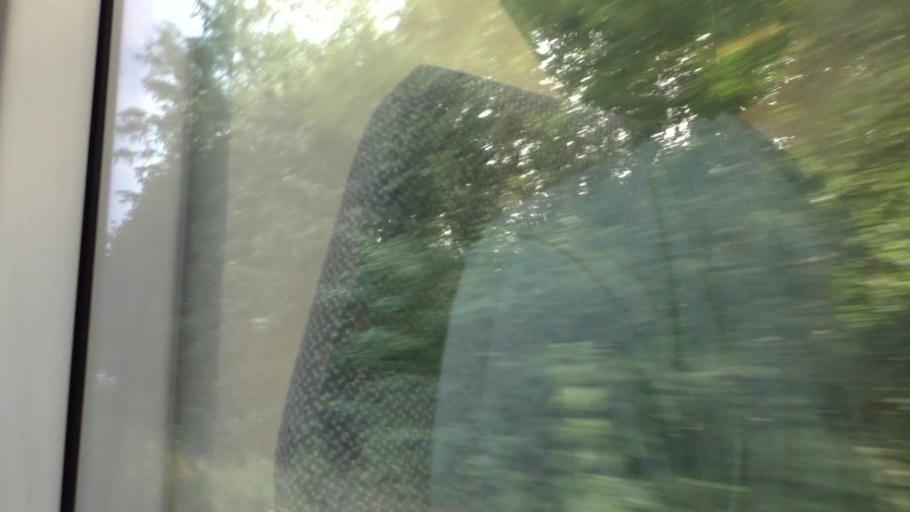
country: DE
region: Brandenburg
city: Konigs Wusterhausen
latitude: 52.2980
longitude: 13.6797
